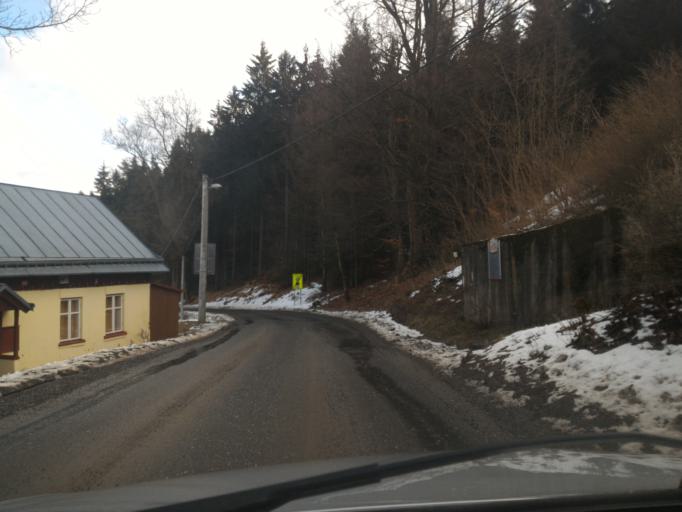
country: CZ
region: Liberecky
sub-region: Okres Jablonec nad Nisou
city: Desna
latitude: 50.7573
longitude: 15.2949
